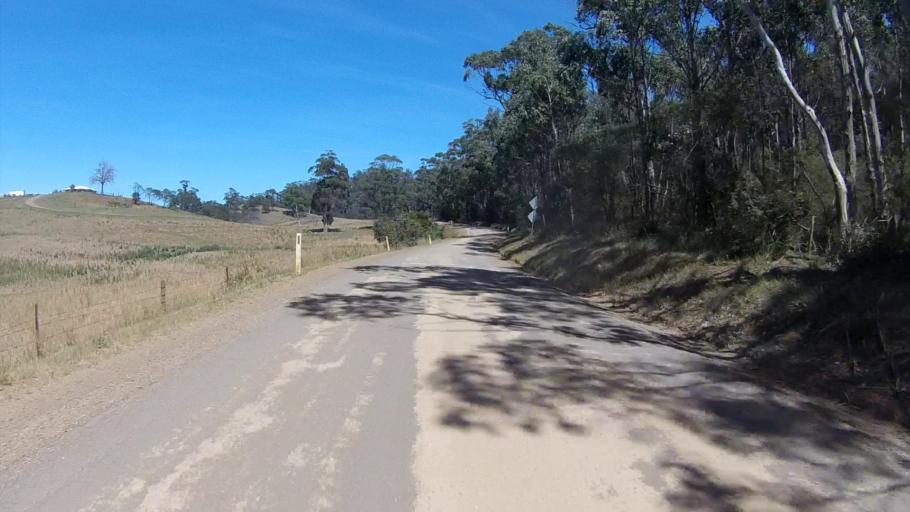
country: AU
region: Tasmania
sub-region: Sorell
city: Sorell
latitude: -42.7530
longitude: 147.6905
